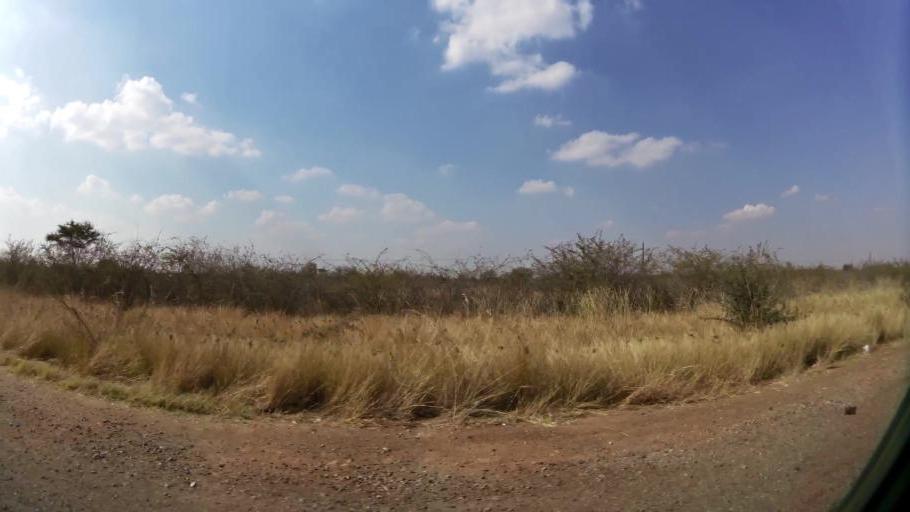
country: ZA
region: North-West
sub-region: Bojanala Platinum District Municipality
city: Rustenburg
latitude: -25.5122
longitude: 27.1002
